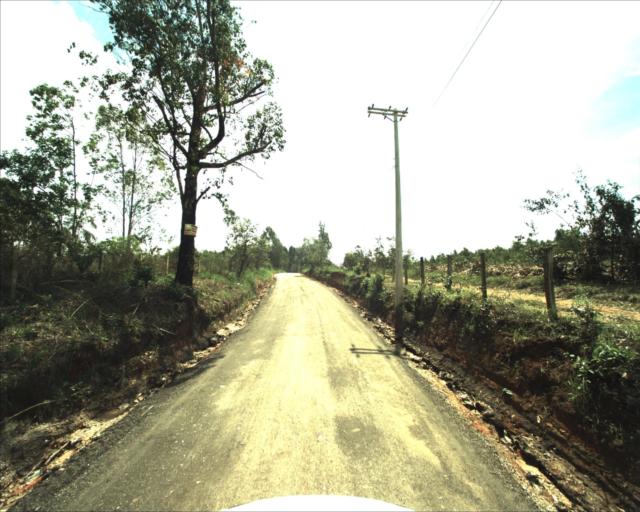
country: BR
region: Sao Paulo
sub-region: Aracoiaba Da Serra
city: Aracoiaba da Serra
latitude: -23.5547
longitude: -47.5388
